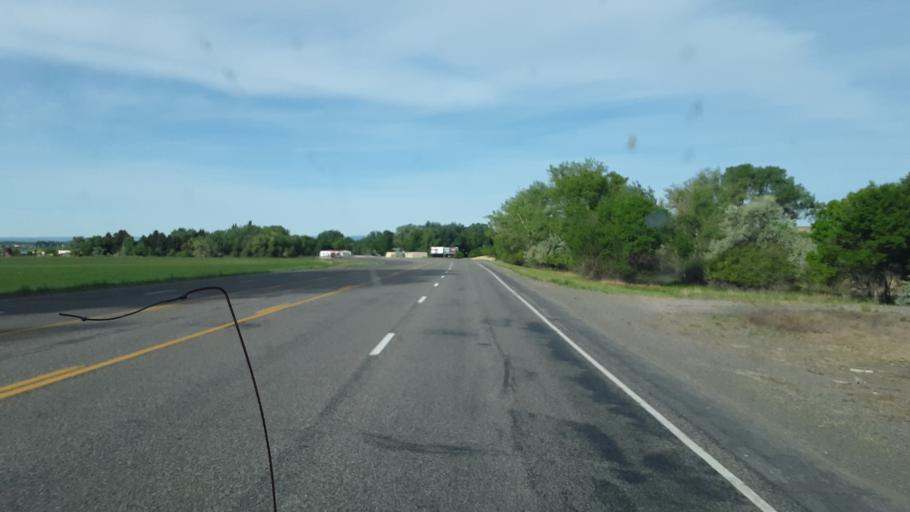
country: US
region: Wyoming
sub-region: Fremont County
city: Riverton
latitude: 43.0848
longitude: -108.3765
